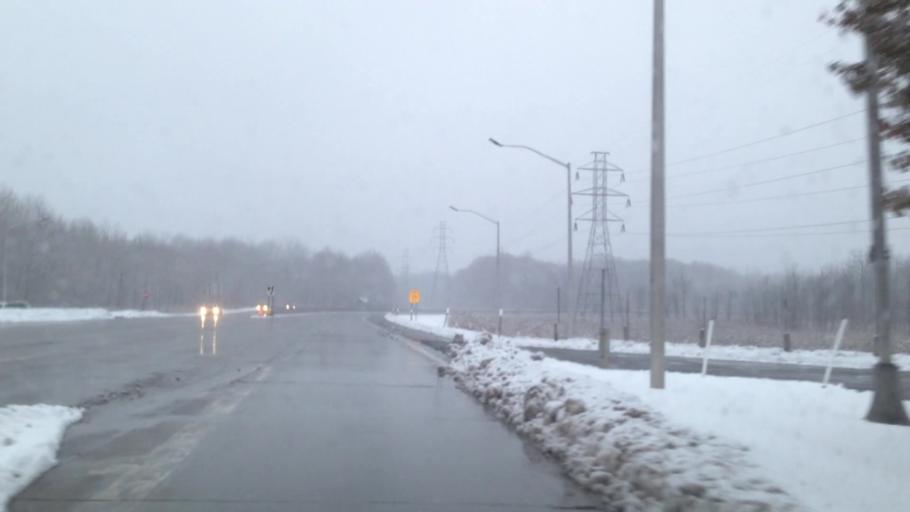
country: US
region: New York
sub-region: Onondaga County
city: East Syracuse
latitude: 43.0983
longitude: -76.0477
